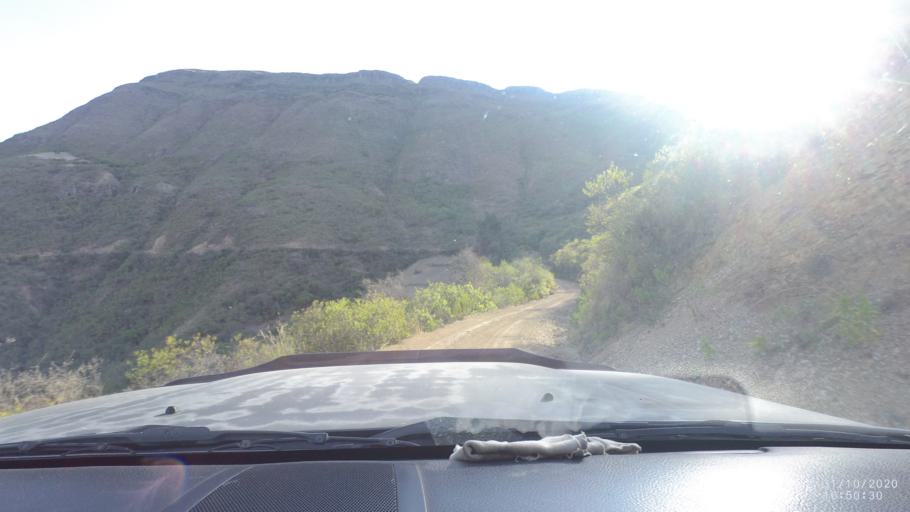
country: BO
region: Chuquisaca
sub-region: Provincia Zudanez
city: Mojocoya
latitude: -18.5090
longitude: -64.5705
